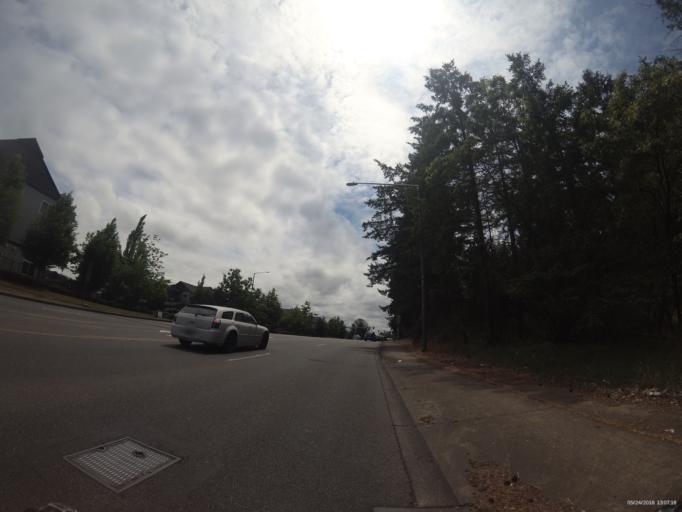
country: US
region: Washington
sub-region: Pierce County
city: Lakewood
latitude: 47.1778
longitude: -122.5079
